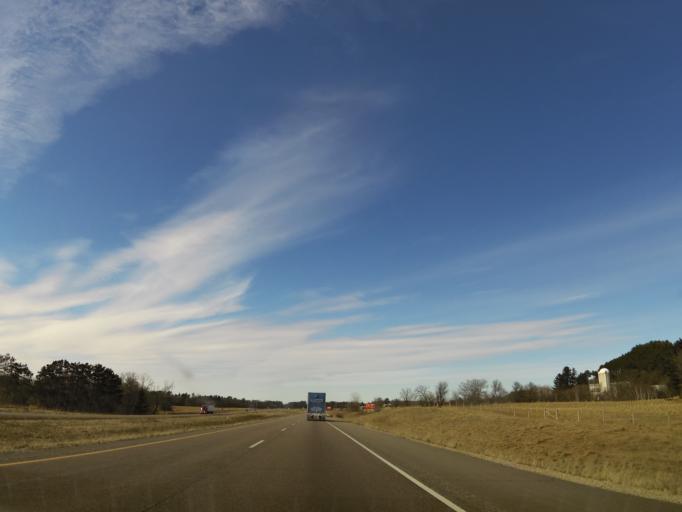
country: US
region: Wisconsin
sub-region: Eau Claire County
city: Fall Creek
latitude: 44.7363
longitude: -91.3710
